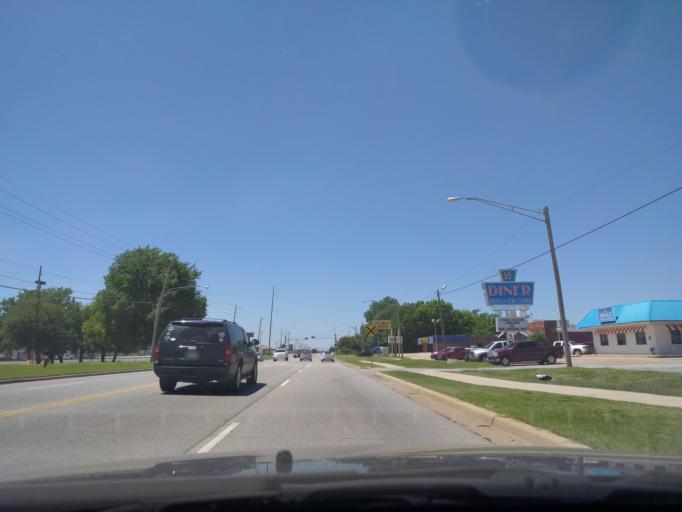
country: US
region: Oklahoma
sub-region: Tulsa County
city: Broken Arrow
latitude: 36.0610
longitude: -95.8094
